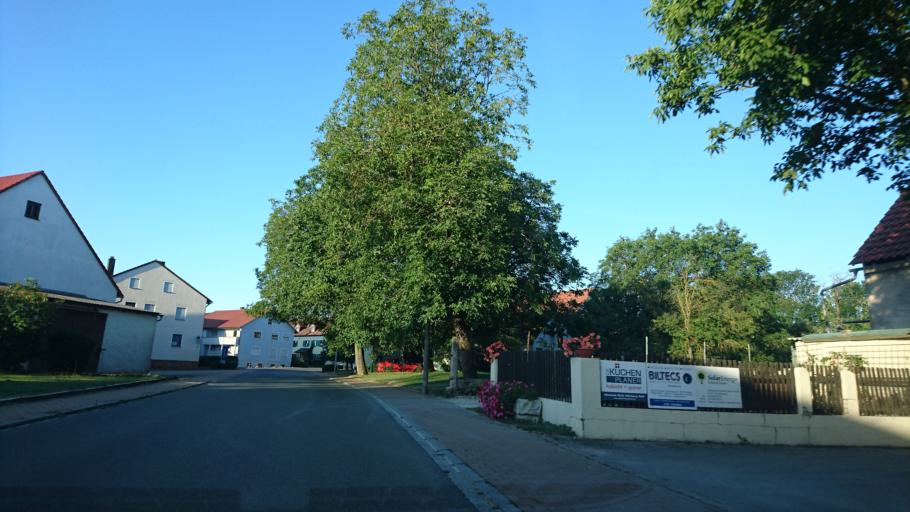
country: DE
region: Bavaria
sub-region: Regierungsbezirk Mittelfranken
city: Burgsalach
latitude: 49.0345
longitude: 11.1012
